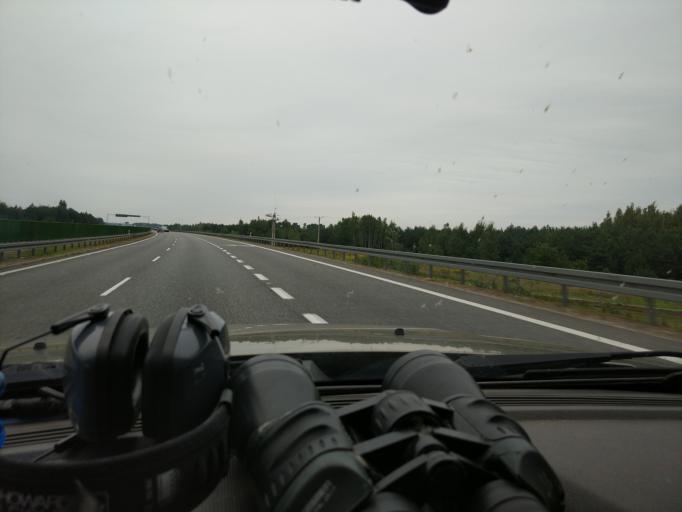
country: PL
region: Masovian Voivodeship
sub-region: Powiat wyszkowski
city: Wyszkow
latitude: 52.5882
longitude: 21.4990
